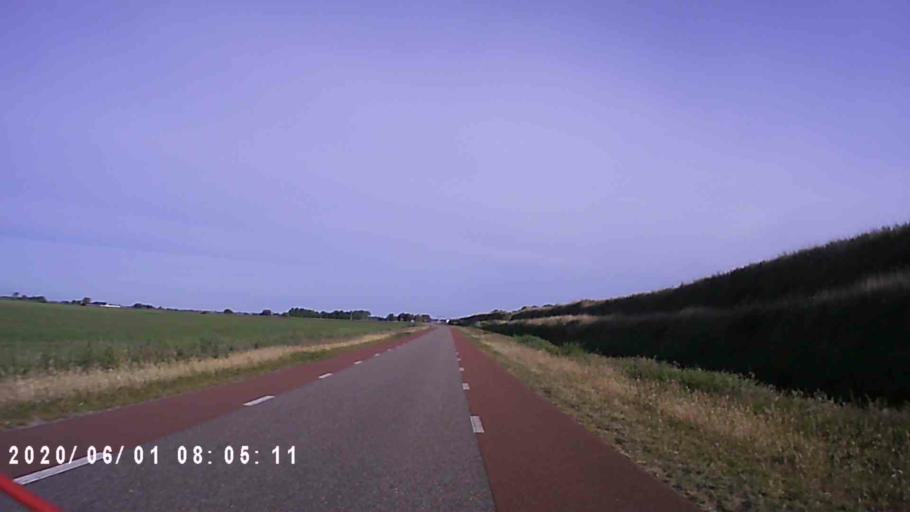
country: NL
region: Friesland
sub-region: Gemeente Tytsjerksteradiel
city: Oentsjerk
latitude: 53.2784
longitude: 5.9119
